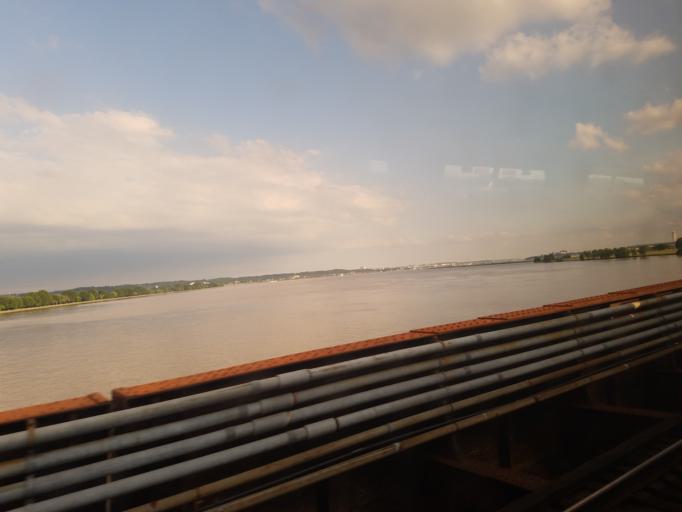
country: US
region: Washington, D.C.
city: Washington, D.C.
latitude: 38.8758
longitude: -77.0374
